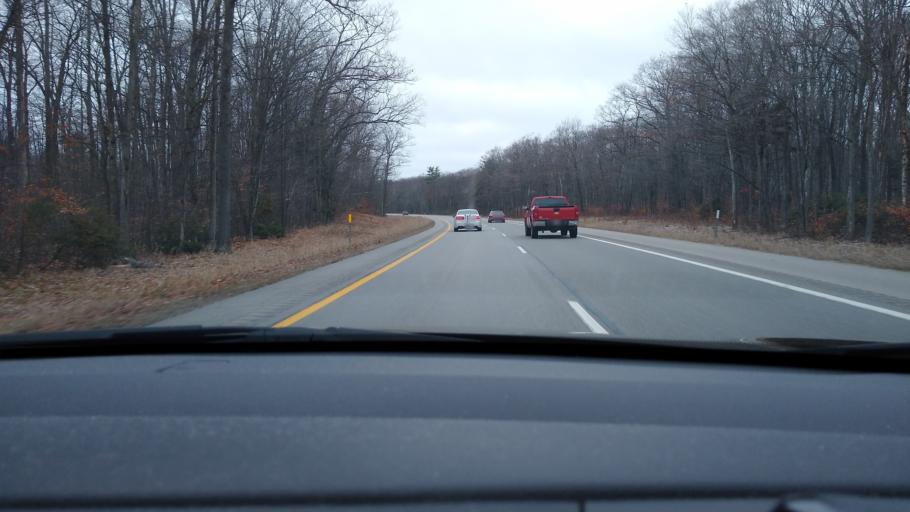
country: US
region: Michigan
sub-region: Otsego County
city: Gaylord
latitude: 44.9444
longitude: -84.6657
